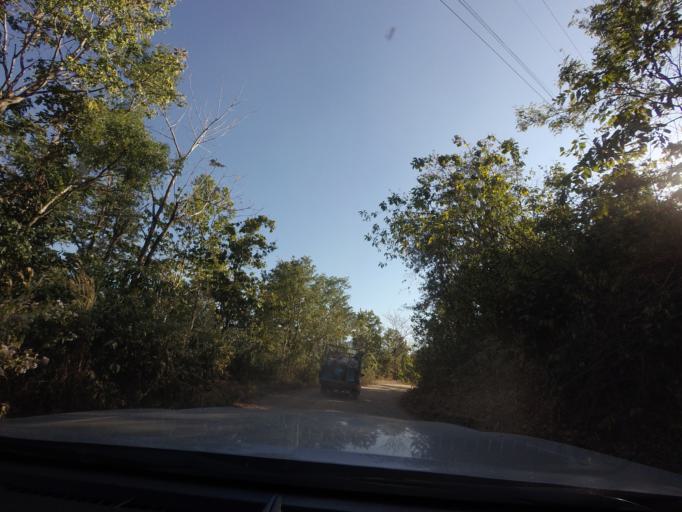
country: TH
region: Lampang
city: Chae Hom
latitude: 18.6143
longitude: 99.6426
